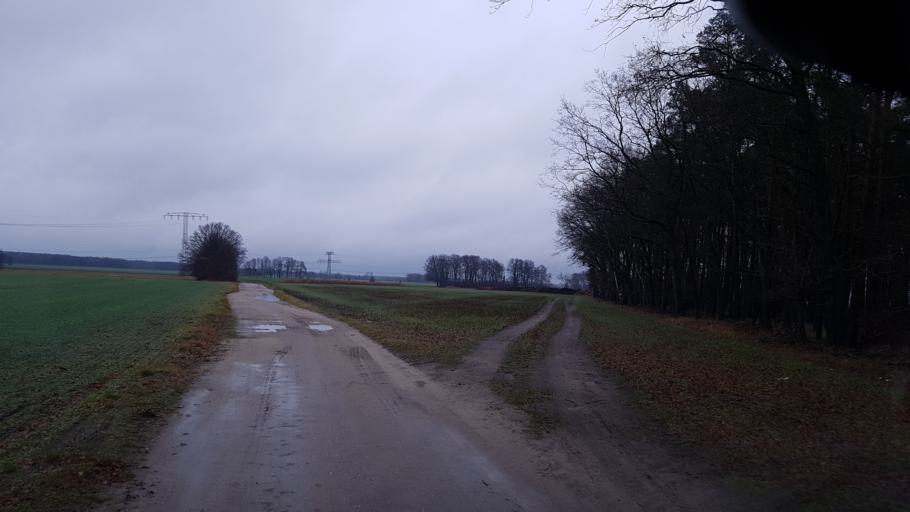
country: DE
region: Brandenburg
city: Sallgast
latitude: 51.6166
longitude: 13.8446
